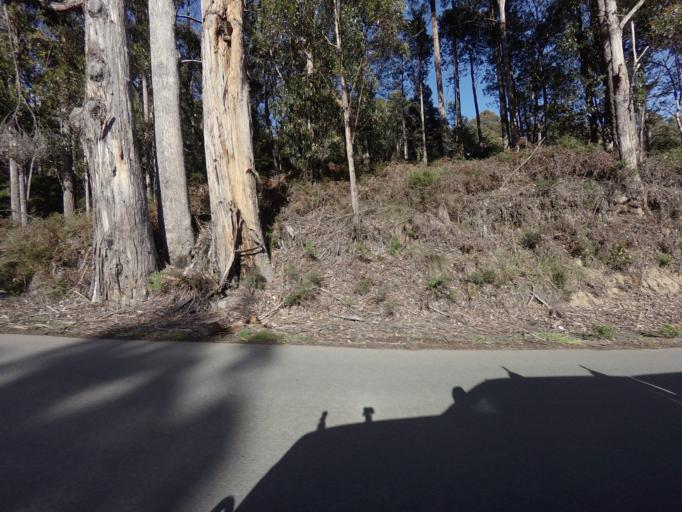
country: AU
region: Tasmania
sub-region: Huon Valley
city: Geeveston
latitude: -43.2507
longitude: 146.9943
